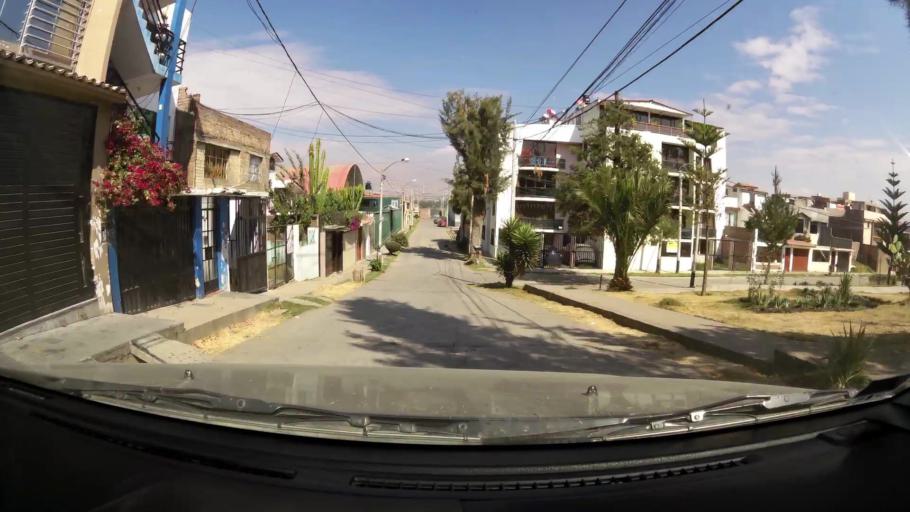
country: PE
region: Junin
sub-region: Provincia de Huancayo
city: El Tambo
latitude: -12.0793
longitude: -75.2282
